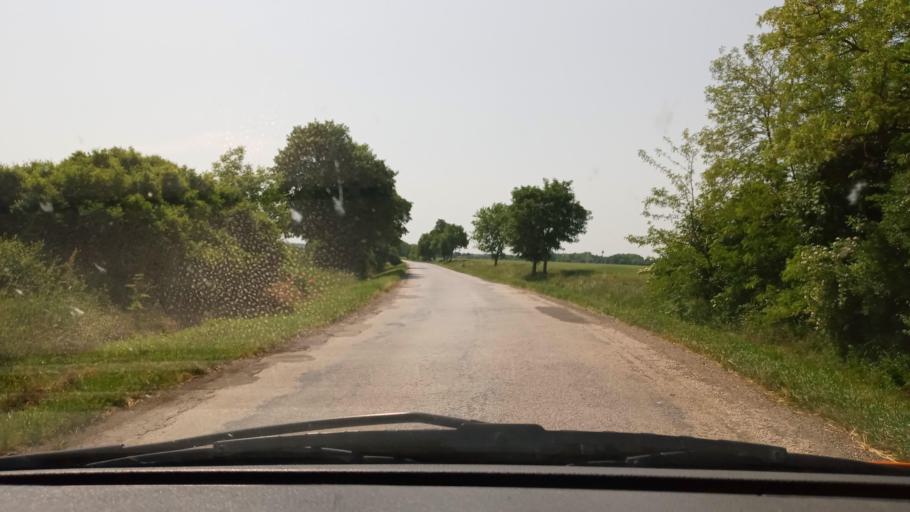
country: HU
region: Baranya
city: Szentlorinc
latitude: 46.0193
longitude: 18.0331
